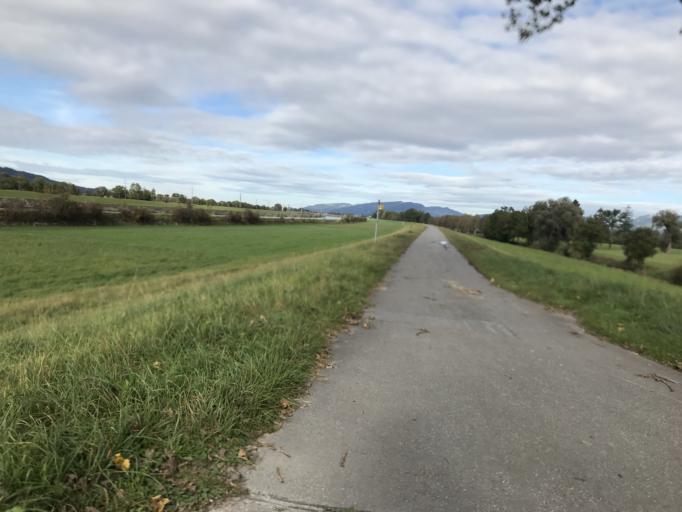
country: AT
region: Vorarlberg
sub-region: Politischer Bezirk Feldkirch
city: Mader
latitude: 47.3687
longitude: 9.6299
